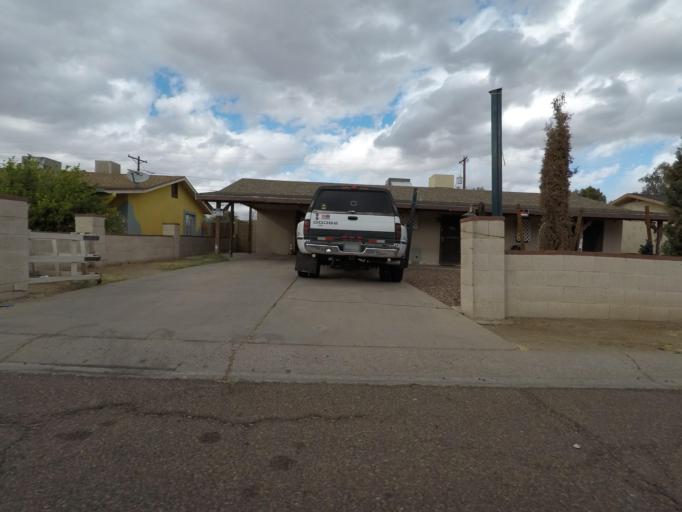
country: US
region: Arizona
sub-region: Maricopa County
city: Glendale
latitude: 33.4986
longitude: -112.1293
